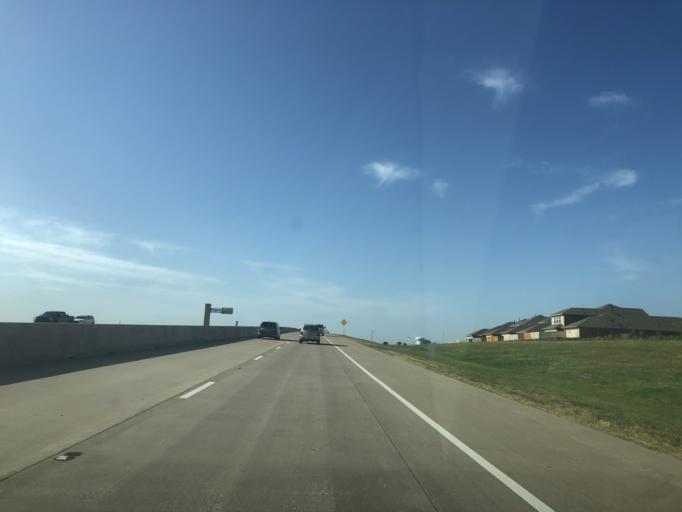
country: US
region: Texas
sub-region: Tarrant County
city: Crowley
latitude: 32.6191
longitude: -97.4127
